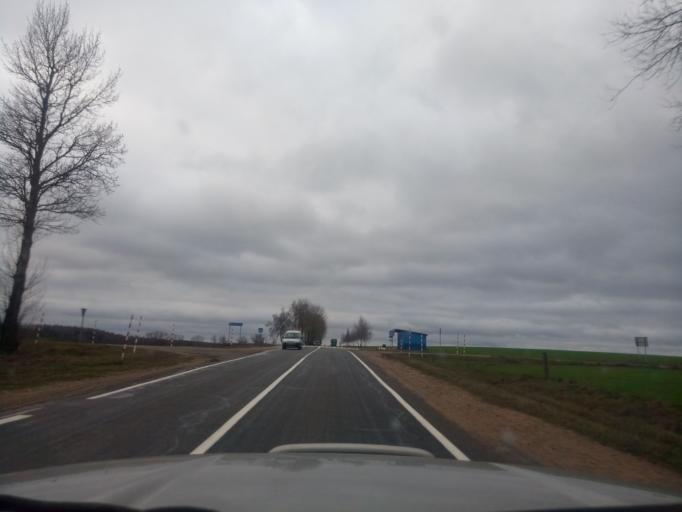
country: BY
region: Minsk
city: Kapyl'
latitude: 53.1829
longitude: 27.1765
